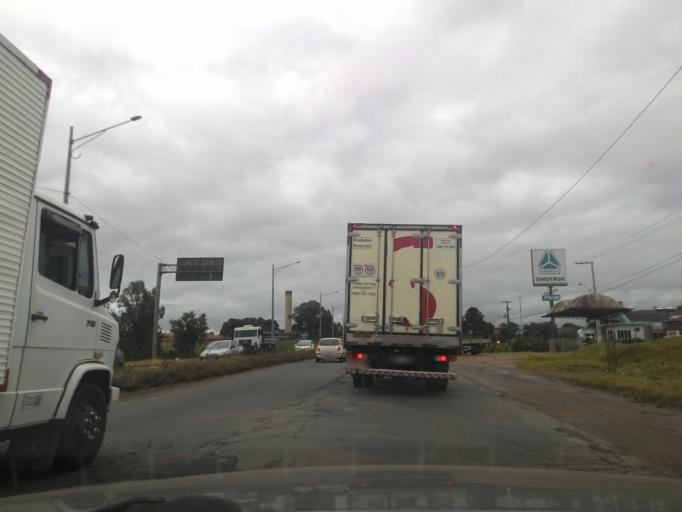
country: BR
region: Parana
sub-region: Sao Jose Dos Pinhais
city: Sao Jose dos Pinhais
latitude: -25.5344
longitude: -49.3008
